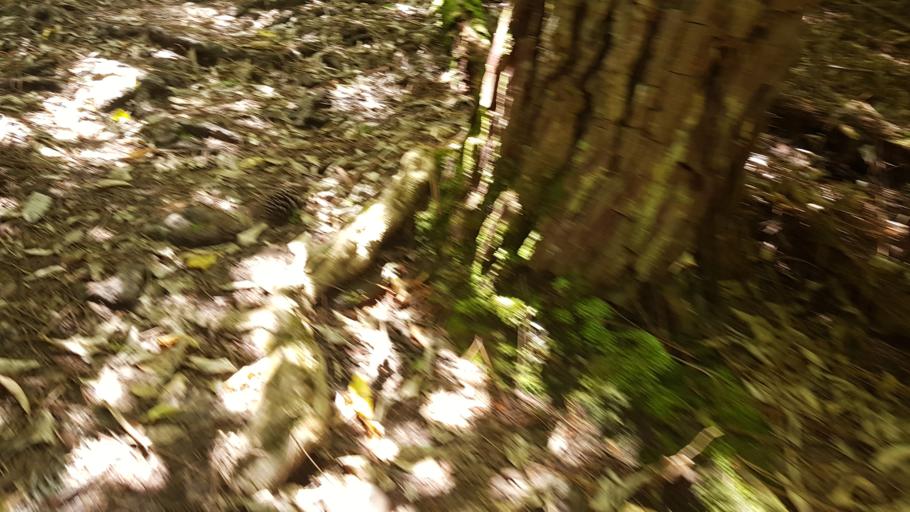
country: NZ
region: Auckland
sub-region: Auckland
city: North Shore
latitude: -36.8245
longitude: 174.7106
